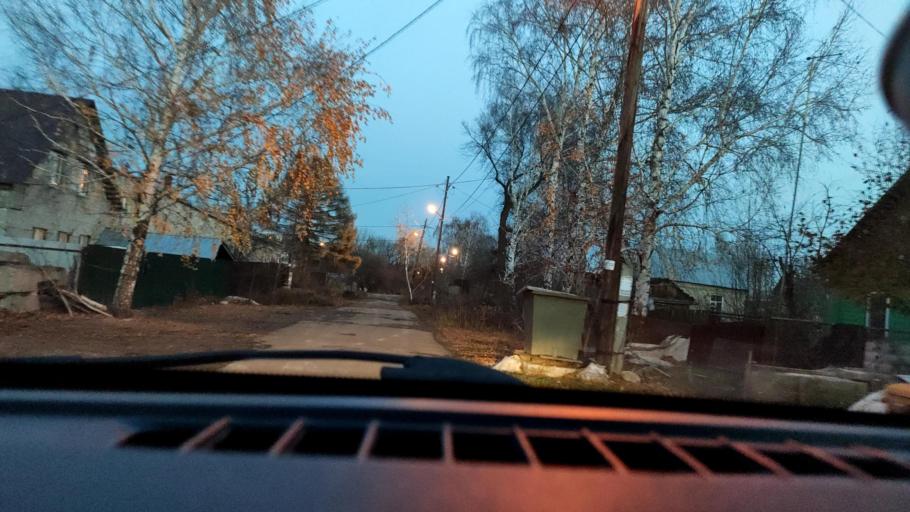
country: RU
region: Samara
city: Petra-Dubrava
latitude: 53.2629
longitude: 50.3335
